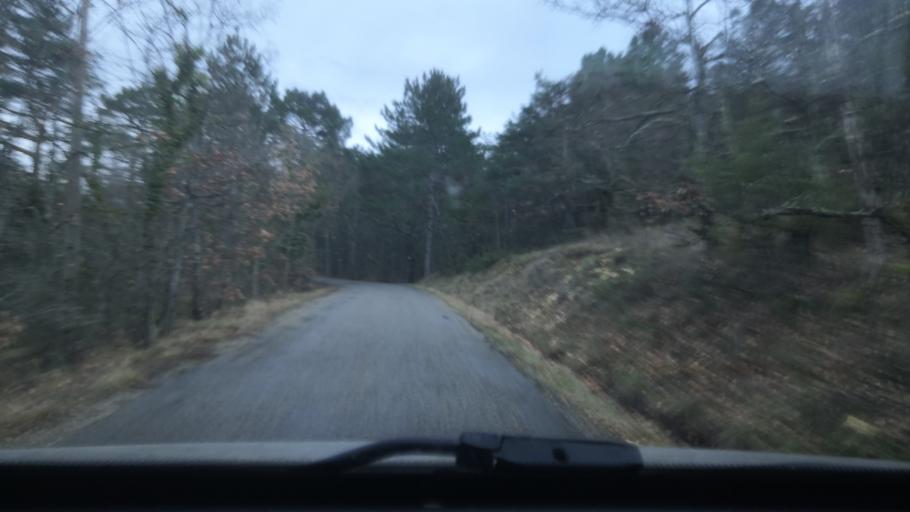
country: FR
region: Rhone-Alpes
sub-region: Departement de la Drome
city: Dieulefit
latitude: 44.5198
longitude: 5.0275
